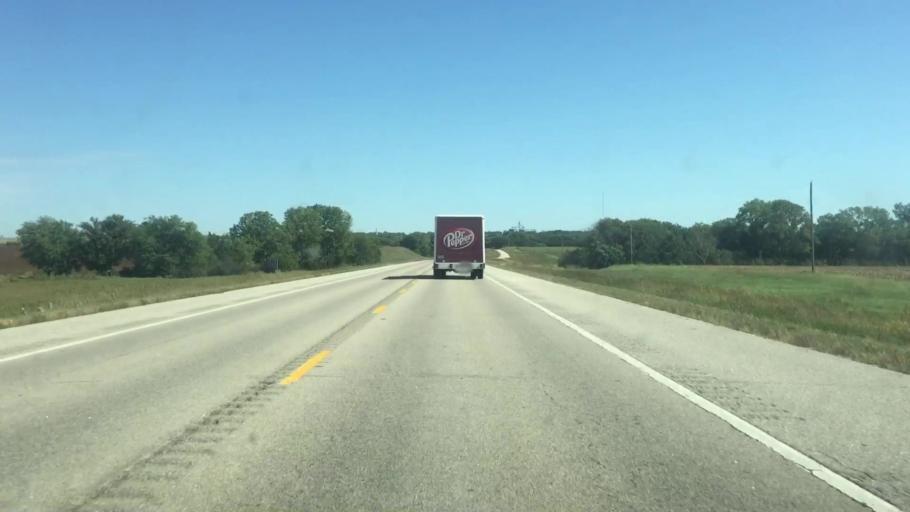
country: US
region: Kansas
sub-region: Marshall County
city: Marysville
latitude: 39.8426
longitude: -96.5503
